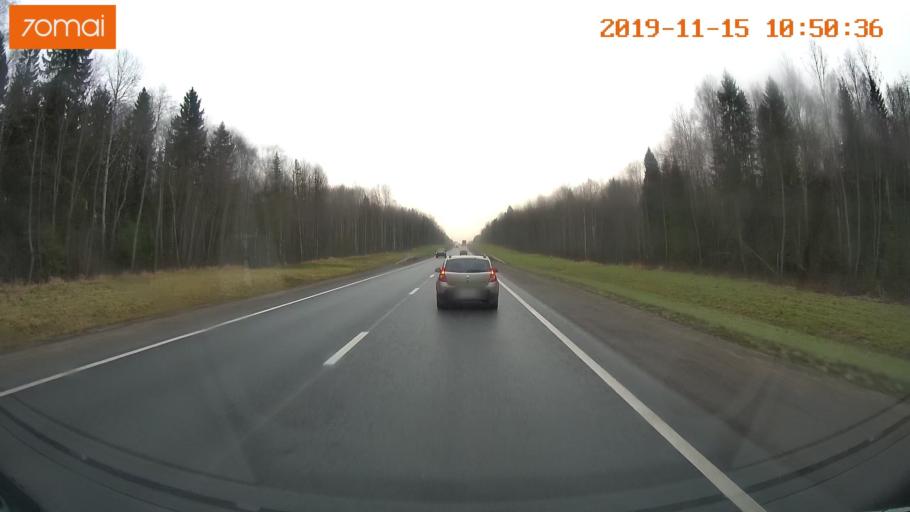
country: RU
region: Vologda
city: Chebsara
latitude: 59.1844
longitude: 38.6856
